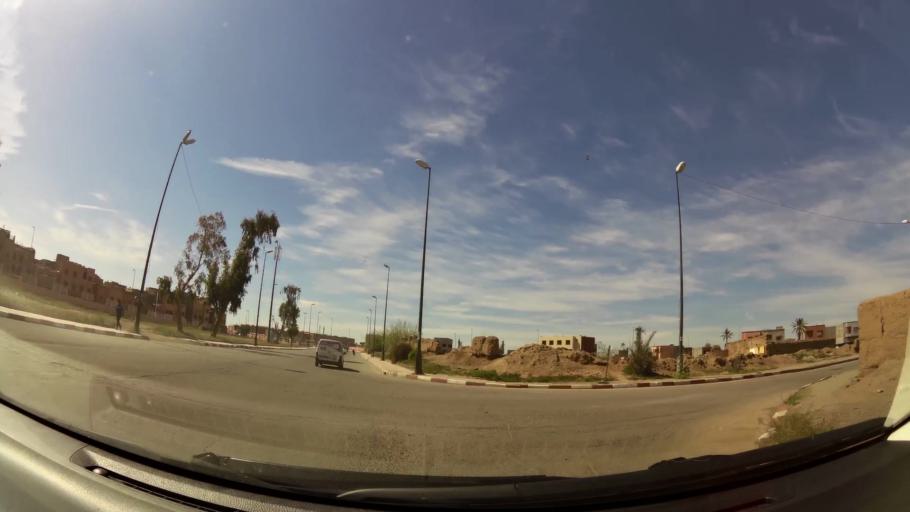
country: MA
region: Marrakech-Tensift-Al Haouz
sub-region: Marrakech
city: Marrakesh
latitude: 31.6216
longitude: -7.9674
